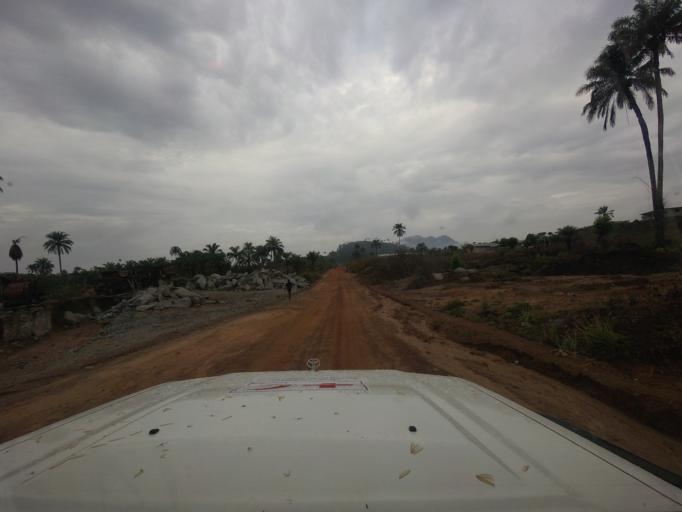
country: LR
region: Lofa
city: Voinjama
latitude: 8.4124
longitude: -9.7714
